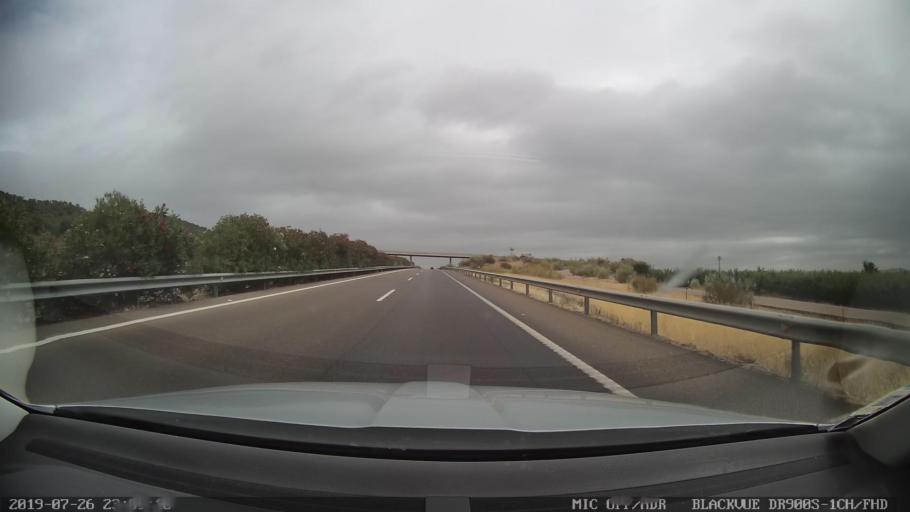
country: ES
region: Extremadura
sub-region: Provincia de Badajoz
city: San Pedro de Merida
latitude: 38.9692
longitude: -6.1513
